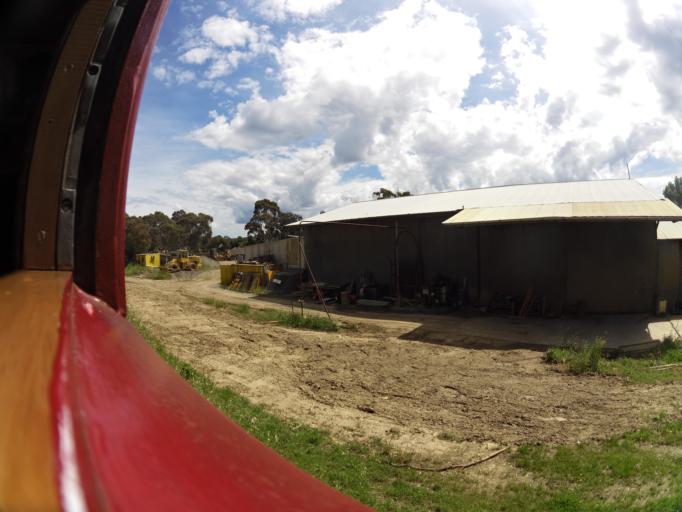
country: AU
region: Victoria
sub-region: Mount Alexander
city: Castlemaine
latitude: -37.0724
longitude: 144.2034
